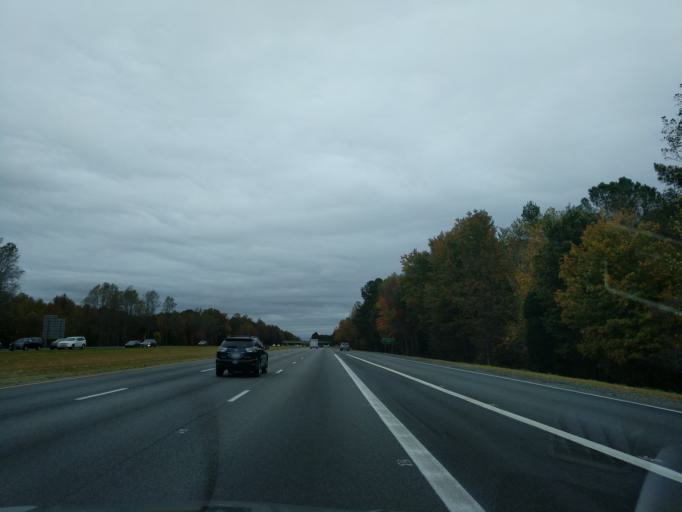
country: US
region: North Carolina
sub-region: Davidson County
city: Lexington
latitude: 35.8123
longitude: -80.1795
